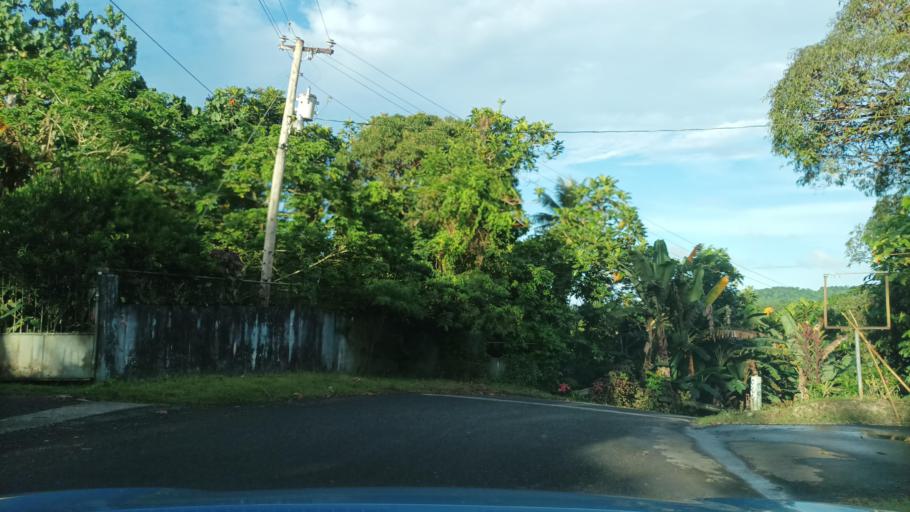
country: FM
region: Pohnpei
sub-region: Kolonia Municipality
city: Kolonia Town
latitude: 6.9669
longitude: 158.2046
